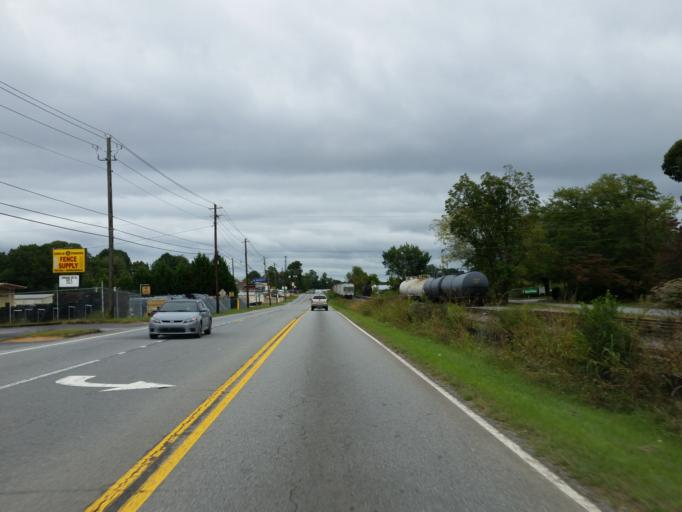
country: US
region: Georgia
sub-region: Cobb County
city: Marietta
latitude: 33.9886
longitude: -84.5312
